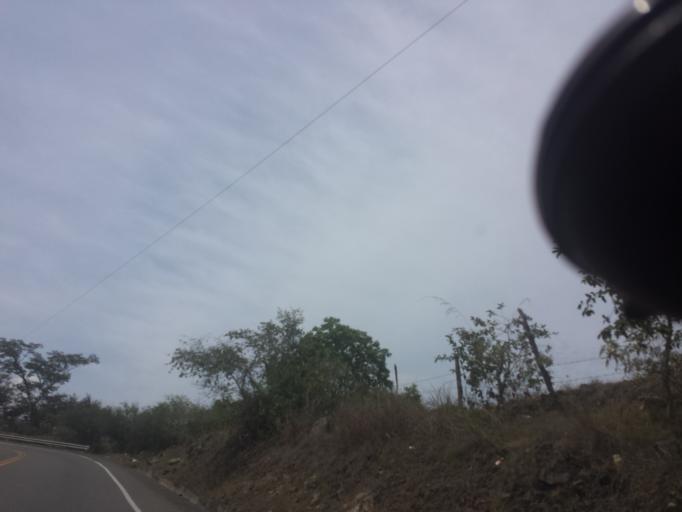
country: CO
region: Antioquia
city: Antioquia
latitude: 6.5782
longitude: -75.8367
